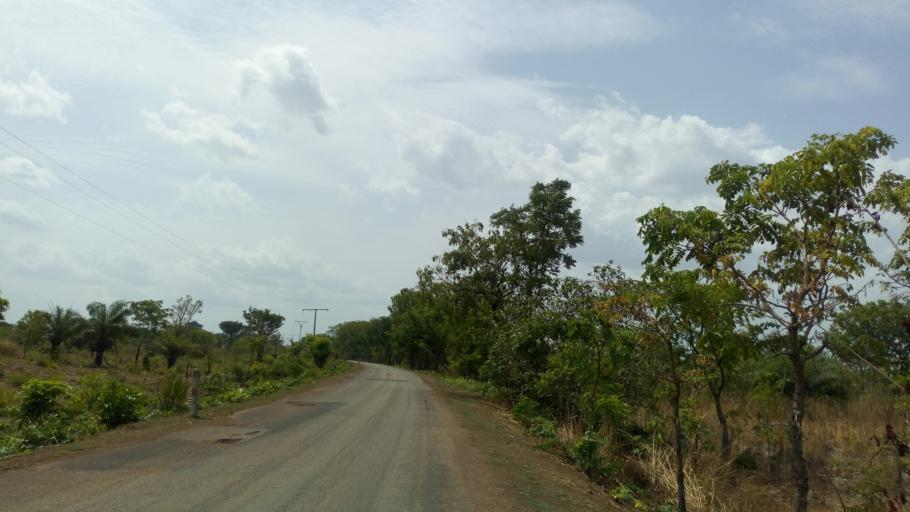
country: TG
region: Centrale
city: Sotouboua
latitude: 8.1576
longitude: 1.0618
